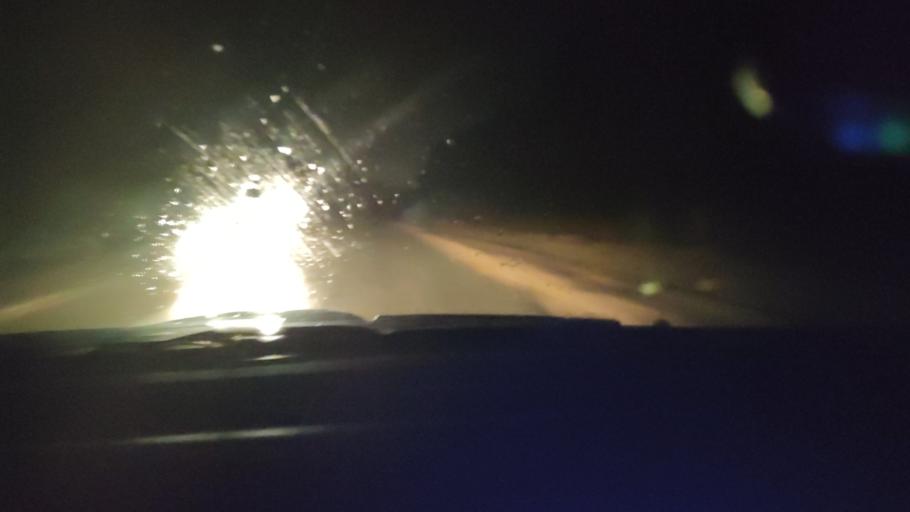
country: RU
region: Udmurtiya
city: Votkinsk
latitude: 57.0902
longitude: 54.0736
